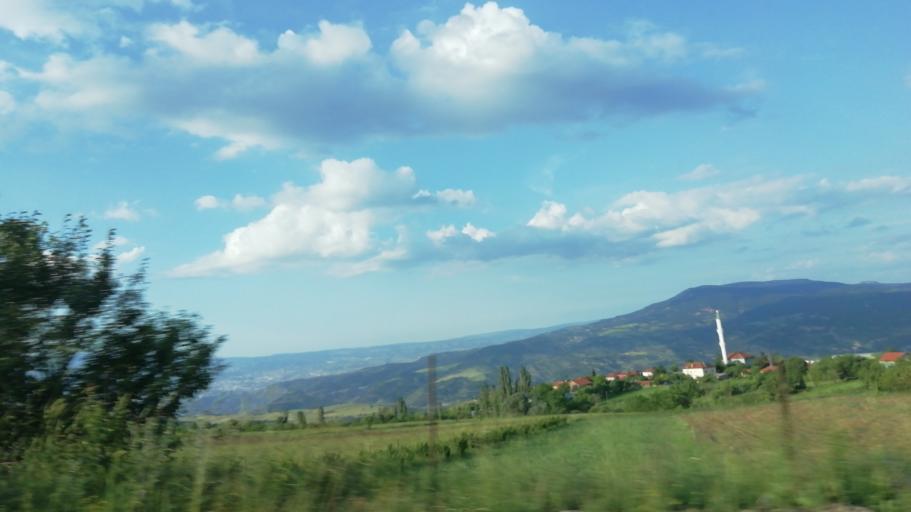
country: TR
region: Karabuk
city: Karabuk
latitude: 41.1253
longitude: 32.6156
